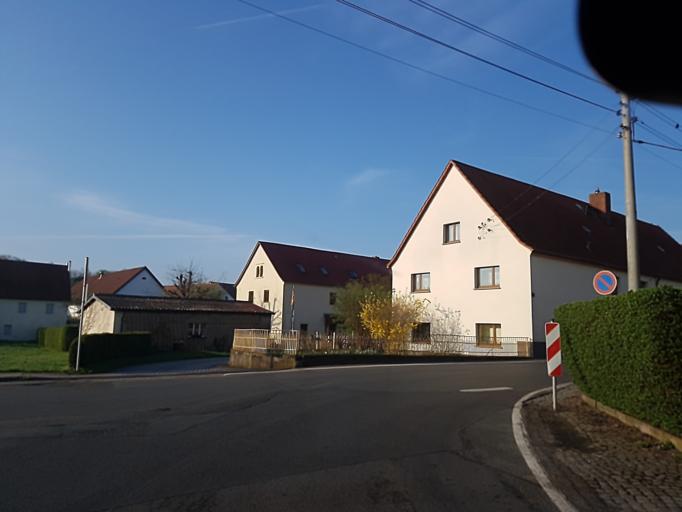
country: DE
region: Saxony
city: Cavertitz
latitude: 51.3867
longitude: 13.1274
